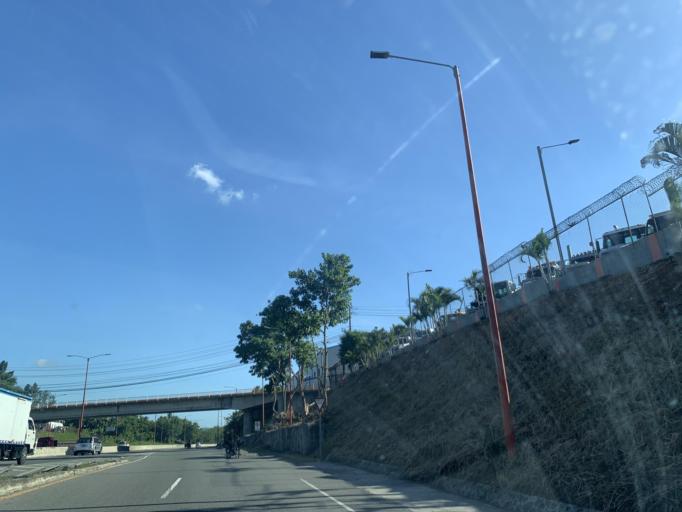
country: DO
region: Santo Domingo
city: Santo Domingo Oeste
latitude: 18.5613
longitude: -70.0696
